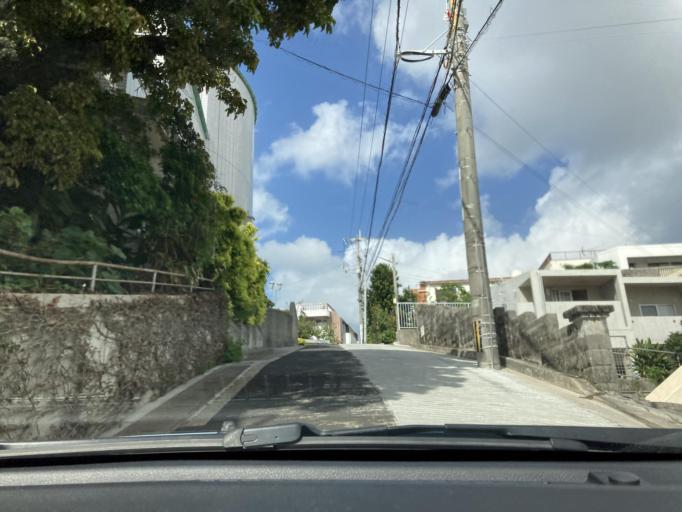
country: JP
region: Okinawa
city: Naha-shi
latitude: 26.2025
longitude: 127.7086
